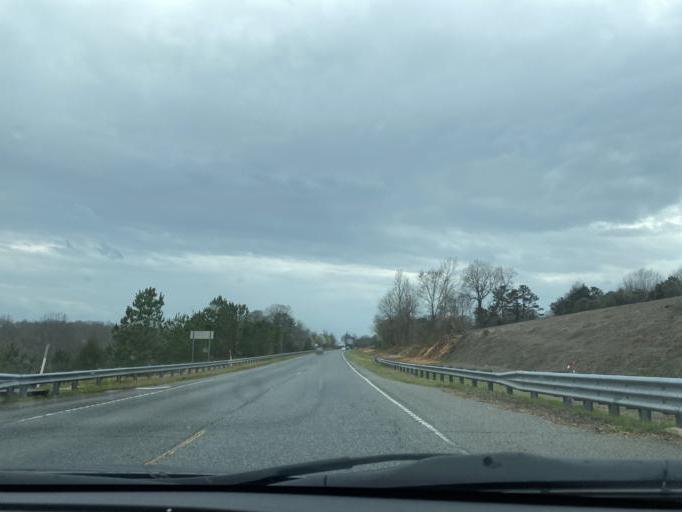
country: US
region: South Carolina
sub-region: Cherokee County
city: Gaffney
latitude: 35.0223
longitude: -81.7162
